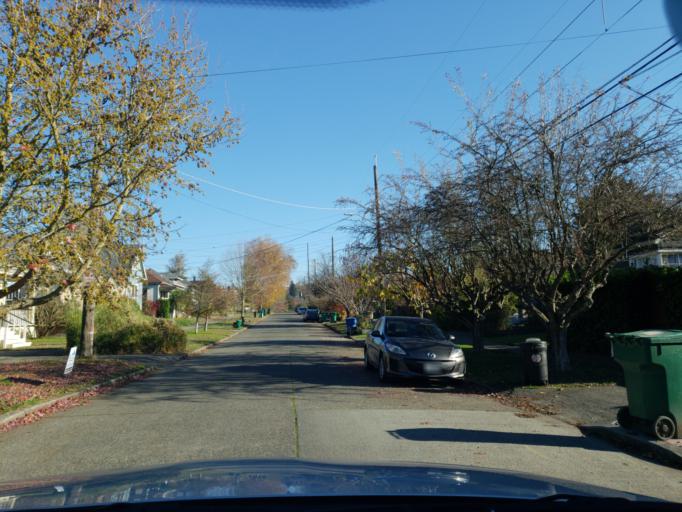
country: US
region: Washington
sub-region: King County
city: Seattle
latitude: 47.6738
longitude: -122.3707
